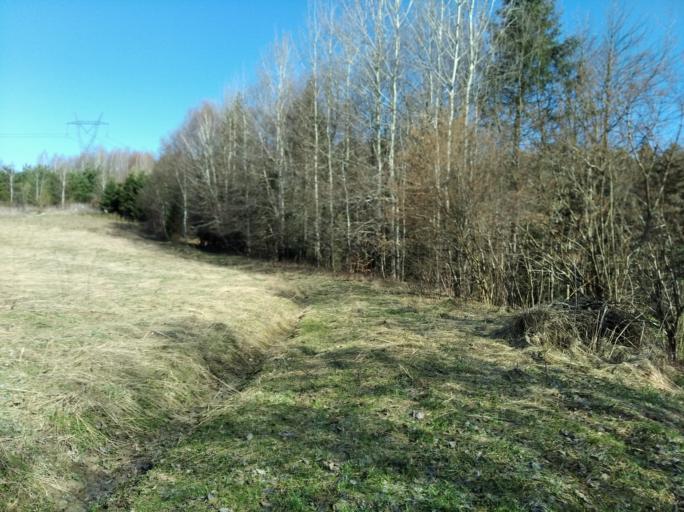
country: PL
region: Subcarpathian Voivodeship
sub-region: Powiat strzyzowski
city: Jawornik
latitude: 49.8352
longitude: 21.8512
